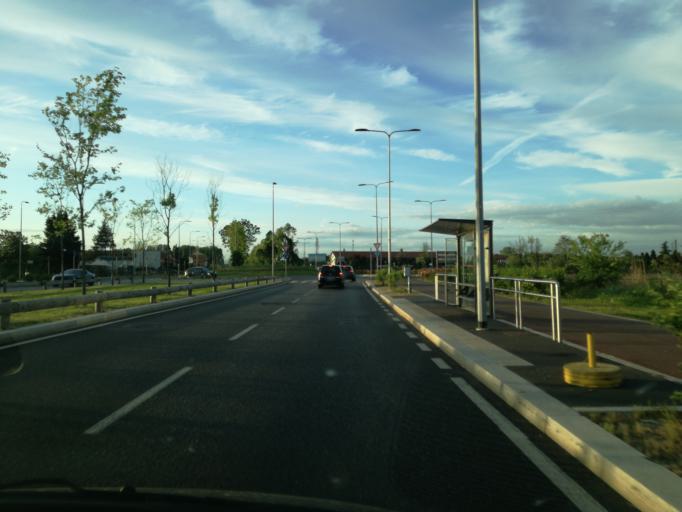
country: IT
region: Lombardy
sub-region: Citta metropolitana di Milano
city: Noverasco-Sporting Mirasole
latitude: 45.4027
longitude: 9.2091
